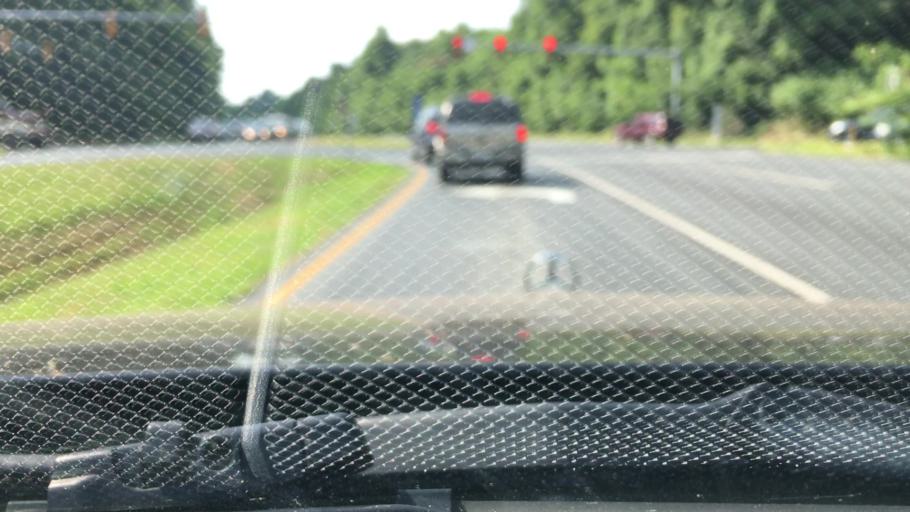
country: US
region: Virginia
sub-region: City of Charlottesville
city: Charlottesville
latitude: 38.0210
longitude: -78.4318
